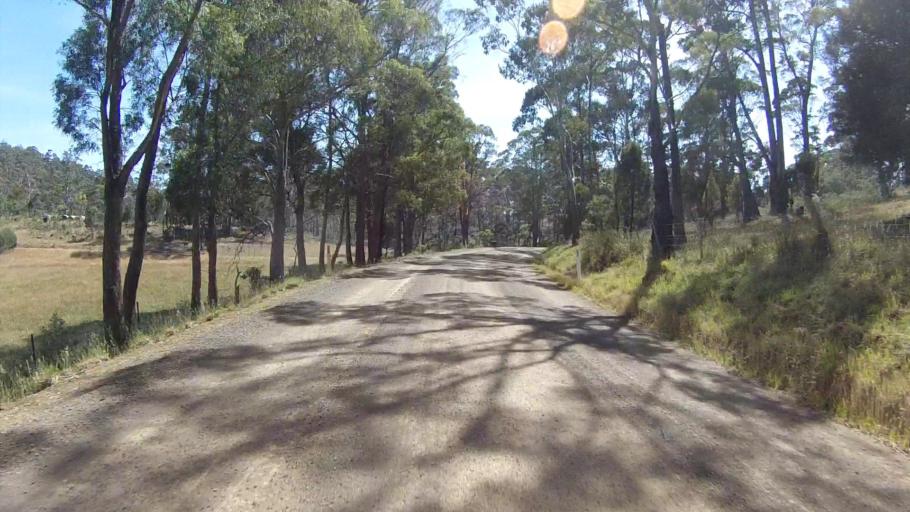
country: AU
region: Tasmania
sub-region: Sorell
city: Sorell
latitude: -42.7513
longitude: 147.7121
